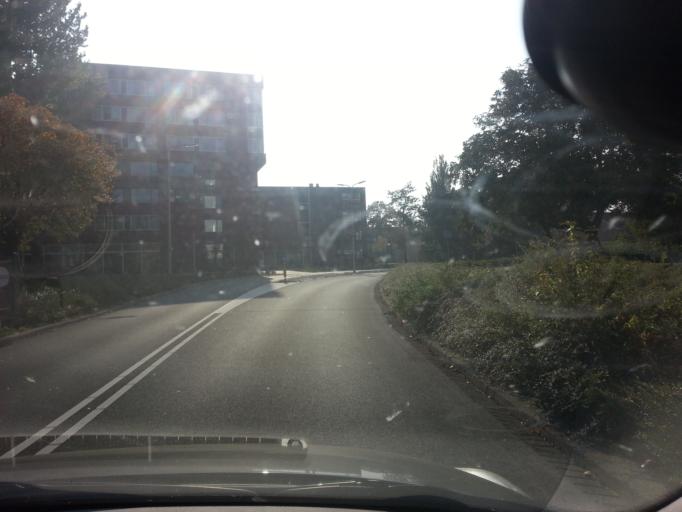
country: NL
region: South Holland
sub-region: Gemeente Zwijndrecht
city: Zwijndrecht
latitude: 51.8236
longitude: 4.6480
